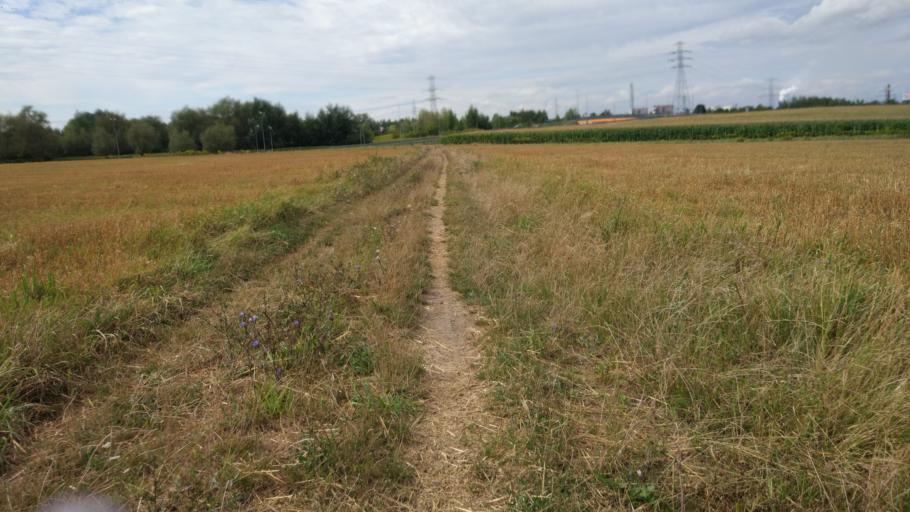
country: PL
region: Masovian Voivodeship
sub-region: Plock
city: Plock
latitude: 52.5295
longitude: 19.7417
